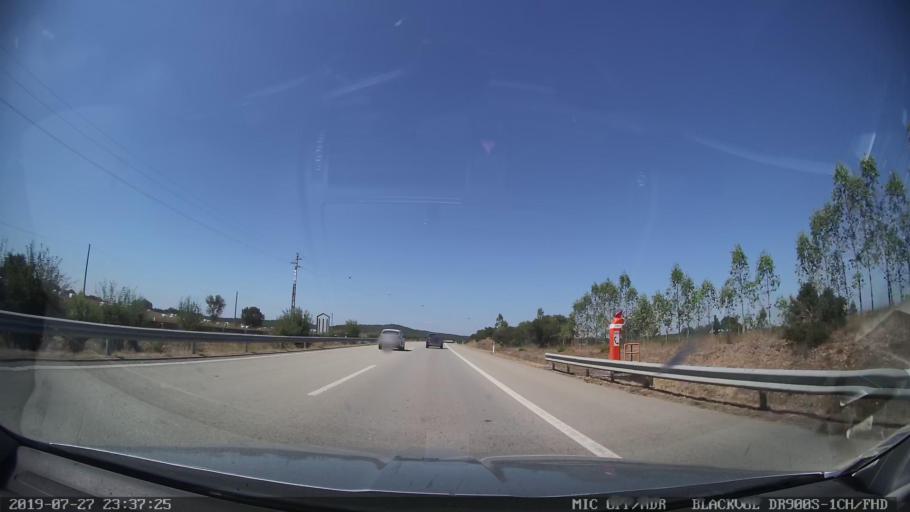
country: PT
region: Evora
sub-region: Montemor-O-Novo
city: Montemor-o-Novo
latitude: 38.6469
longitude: -8.2577
